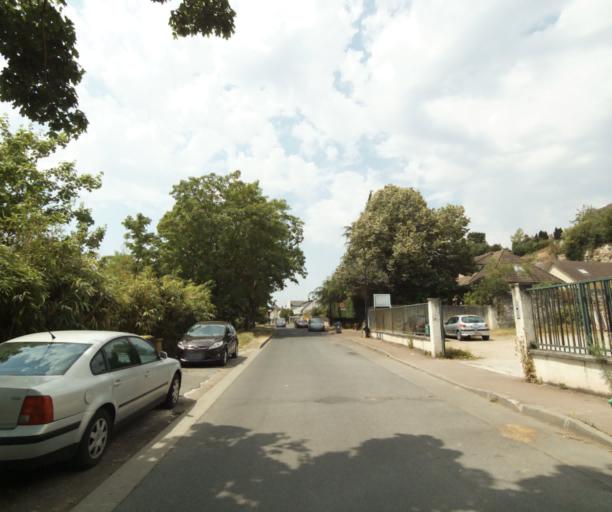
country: FR
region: Ile-de-France
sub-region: Departement des Yvelines
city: Conflans-Sainte-Honorine
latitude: 48.9924
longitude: 2.1211
